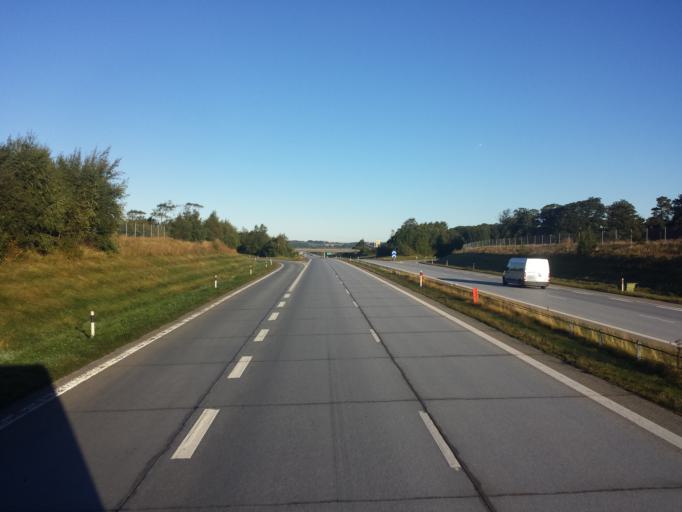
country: SE
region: Halland
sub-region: Falkenbergs Kommun
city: Falkenberg
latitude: 56.8992
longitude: 12.5861
